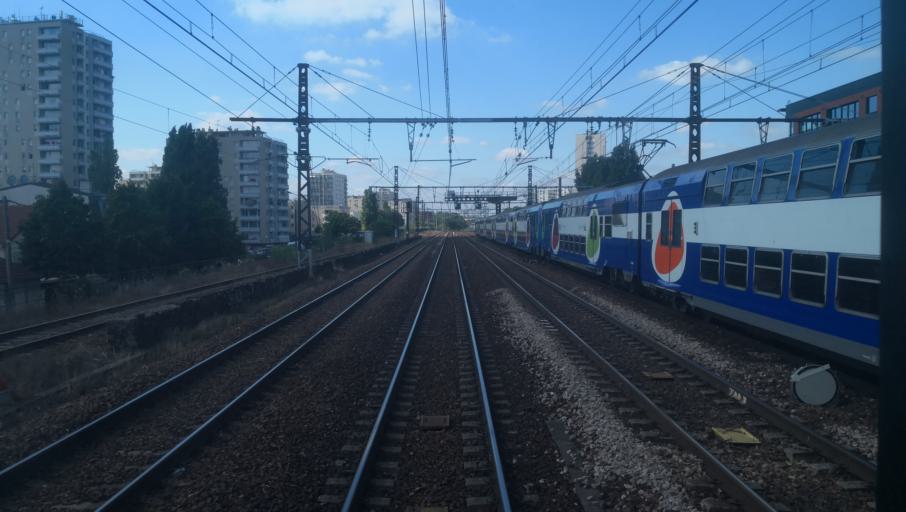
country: FR
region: Ile-de-France
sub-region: Departement du Val-de-Marne
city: Alfortville
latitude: 48.7897
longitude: 2.4315
